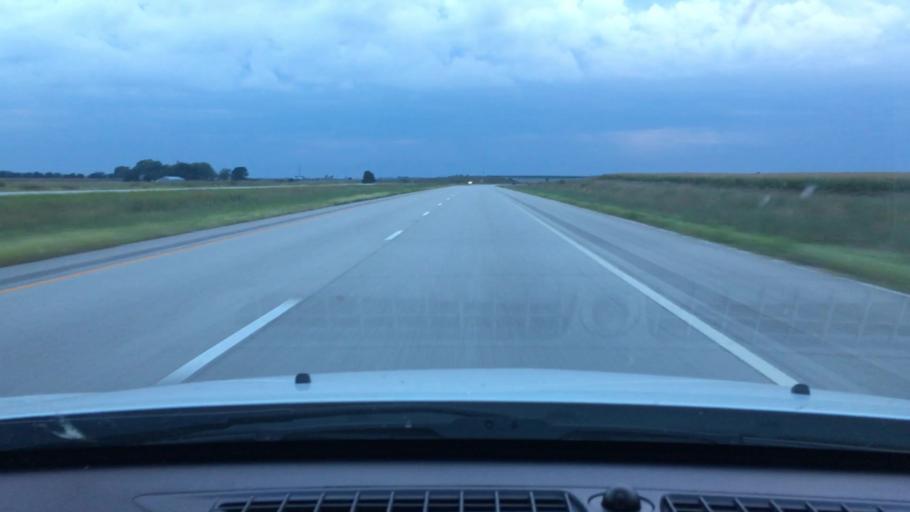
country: US
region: Illinois
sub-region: Sangamon County
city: New Berlin
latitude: 39.7390
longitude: -89.9760
